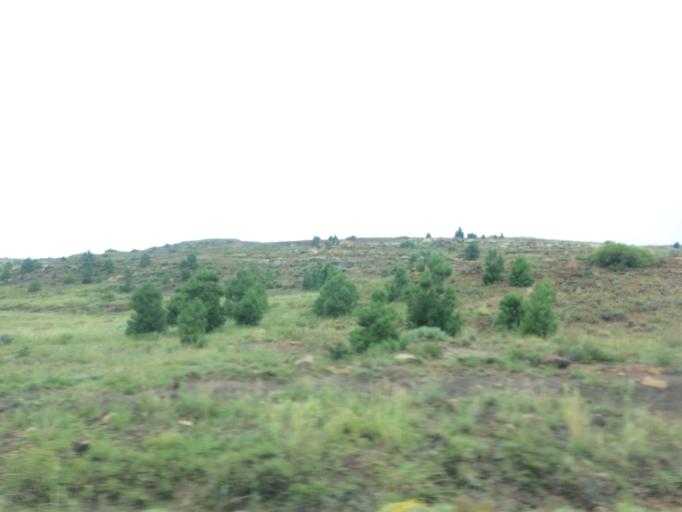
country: LS
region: Maseru
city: Nako
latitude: -29.7591
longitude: 27.5201
